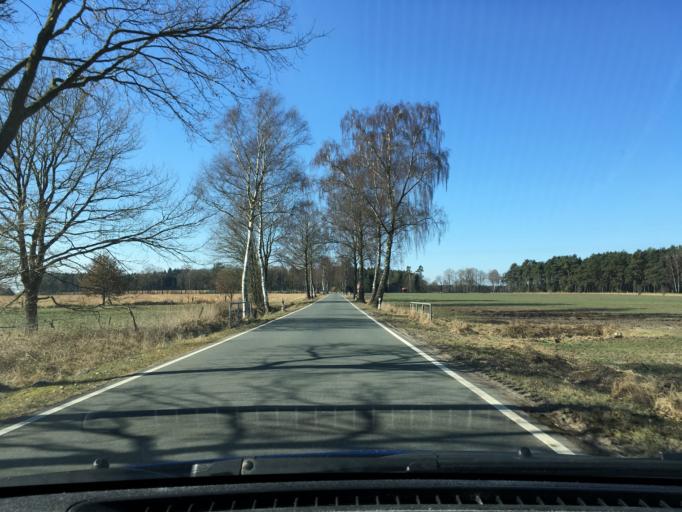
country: DE
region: Lower Saxony
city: Schneverdingen
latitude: 53.0839
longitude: 9.7425
